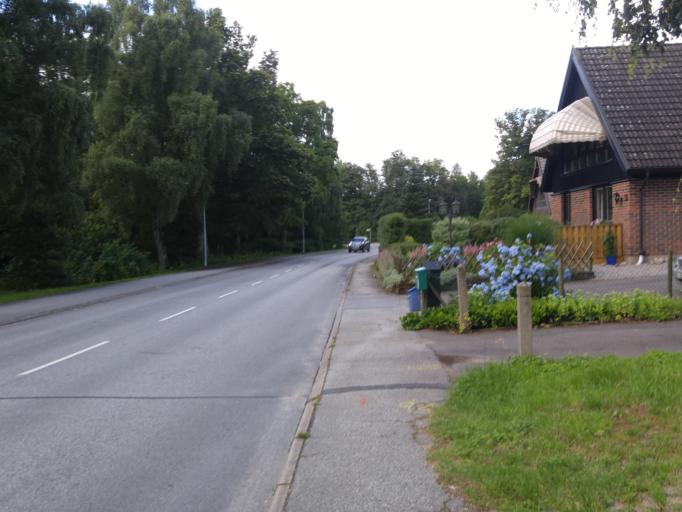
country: SE
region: Skane
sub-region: Hoors Kommun
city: Hoeoer
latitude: 55.9270
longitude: 13.5361
